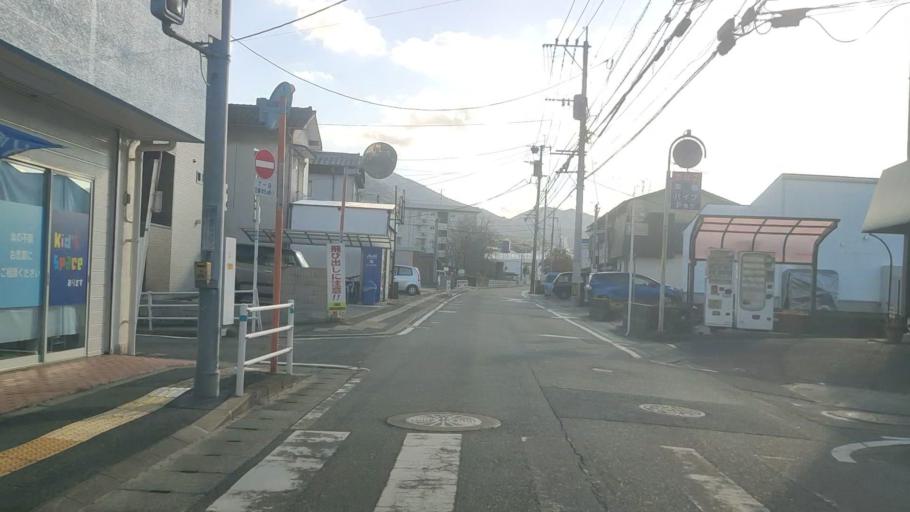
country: JP
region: Fukuoka
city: Fukuoka-shi
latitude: 33.5493
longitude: 130.3574
